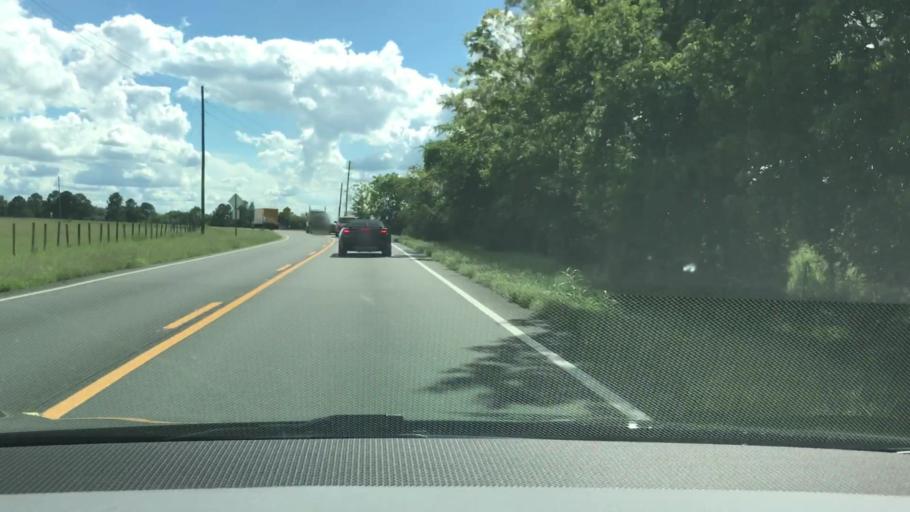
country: US
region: Alabama
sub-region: Montgomery County
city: Pike Road
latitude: 32.3099
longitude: -86.1015
